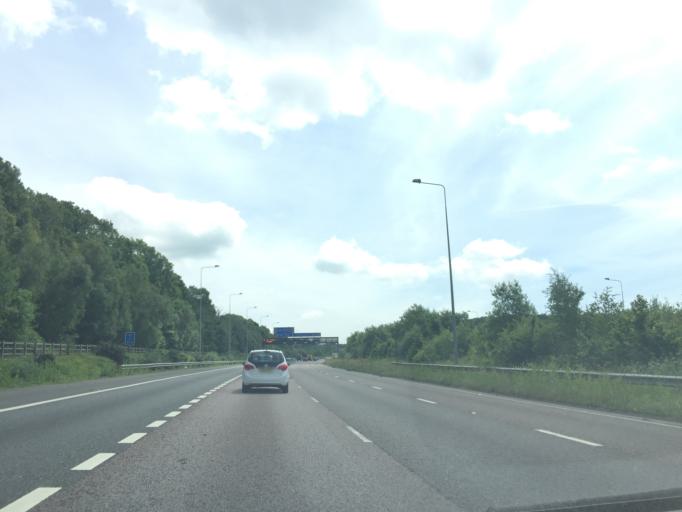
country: GB
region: England
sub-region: Kent
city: Chatham
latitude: 51.3466
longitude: 0.5027
